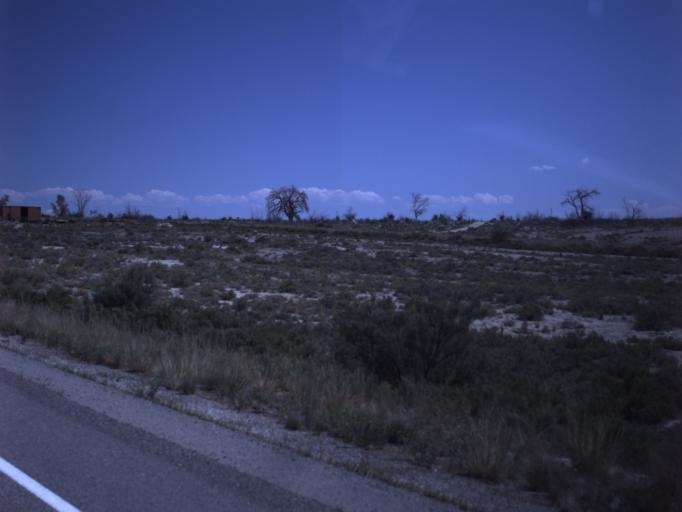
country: US
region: Utah
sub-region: Emery County
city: Ferron
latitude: 39.1053
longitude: -111.1290
